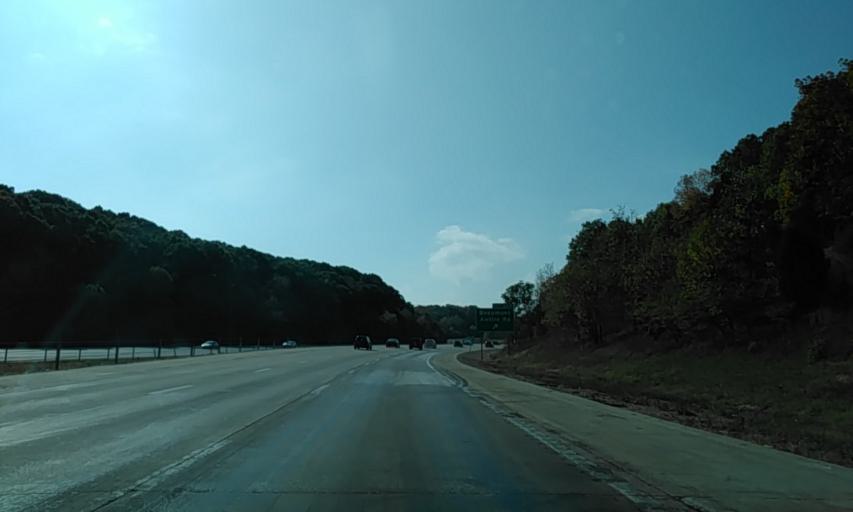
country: US
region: Missouri
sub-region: Saint Louis County
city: Valley Park
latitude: 38.5207
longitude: -90.5459
